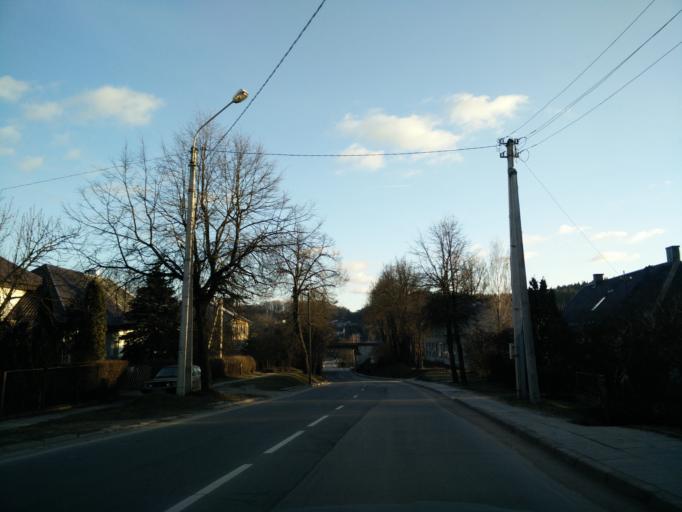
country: LT
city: Skaidiskes
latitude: 54.6945
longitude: 25.3968
